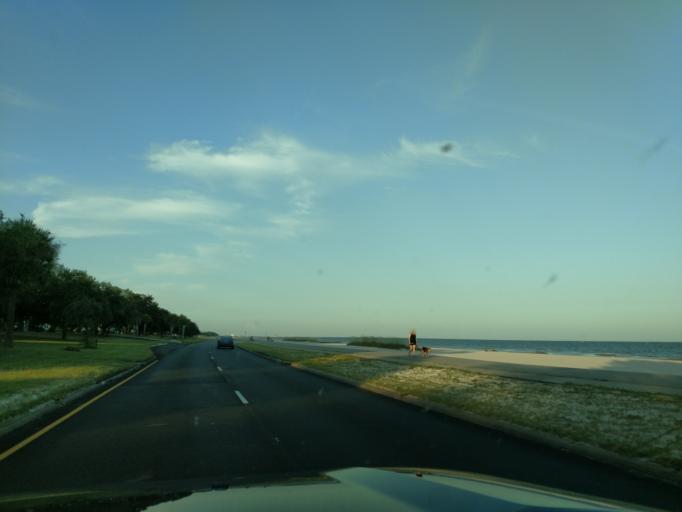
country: US
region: Mississippi
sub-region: Harrison County
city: Gulfport
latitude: 30.3711
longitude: -89.0755
